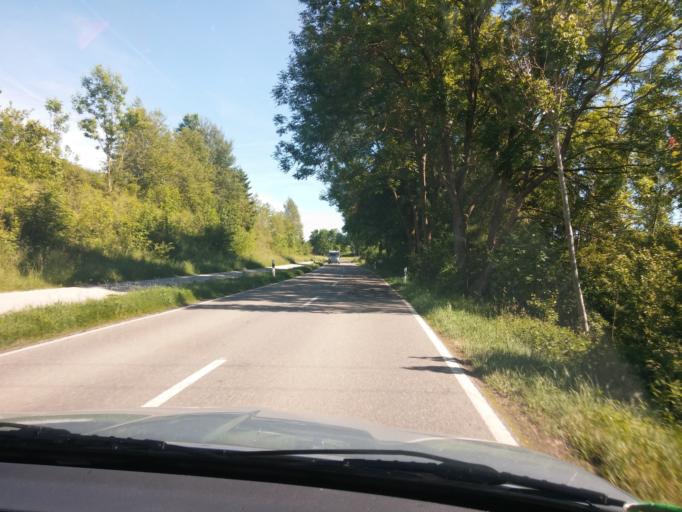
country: DE
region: Bavaria
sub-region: Swabia
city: Woringen
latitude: 47.8878
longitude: 10.2125
